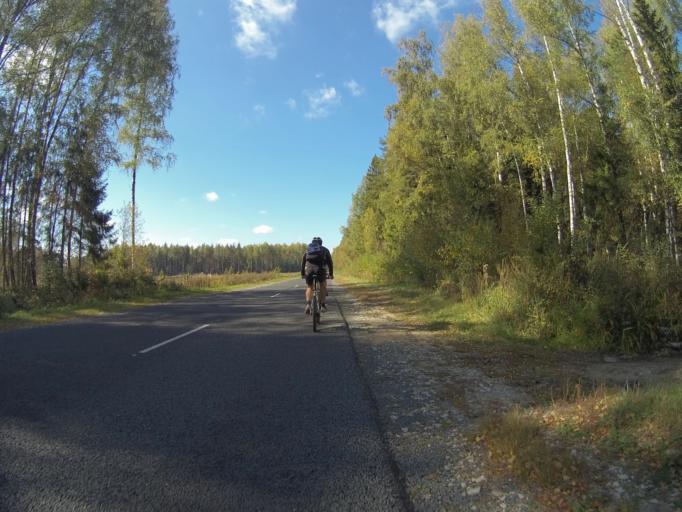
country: RU
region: Vladimir
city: Raduzhnyy
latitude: 55.9838
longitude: 40.2486
